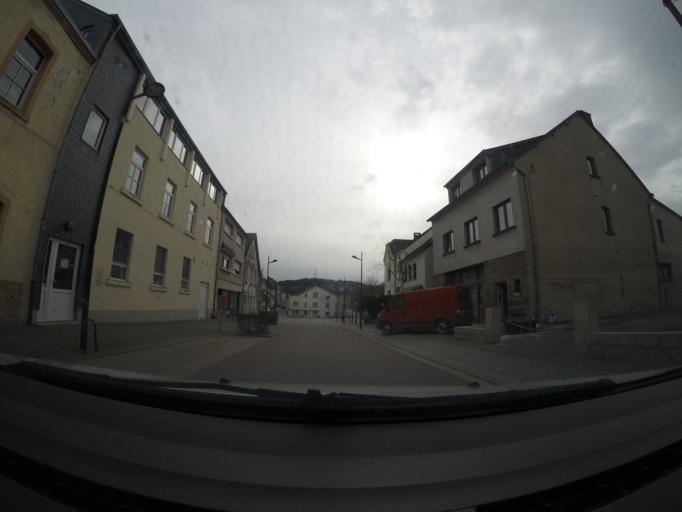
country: BE
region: Wallonia
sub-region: Province du Luxembourg
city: Martelange
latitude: 49.8316
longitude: 5.7387
